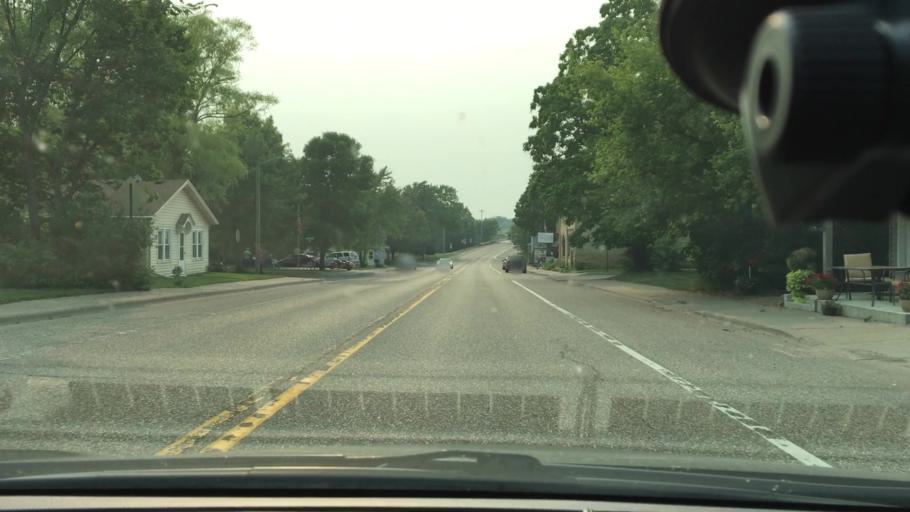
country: US
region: Minnesota
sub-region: Hennepin County
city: Dayton
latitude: 45.2442
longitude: -93.5179
